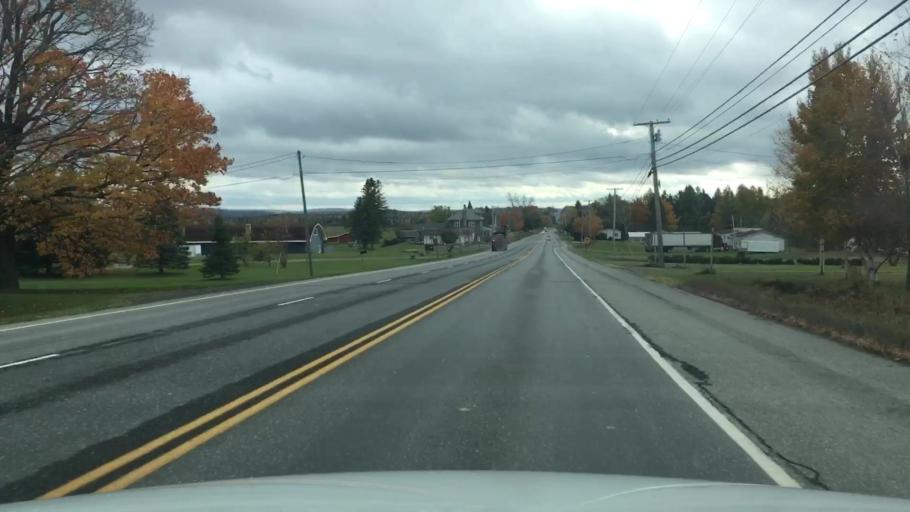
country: US
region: Maine
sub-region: Aroostook County
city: Houlton
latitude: 46.2196
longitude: -67.8410
